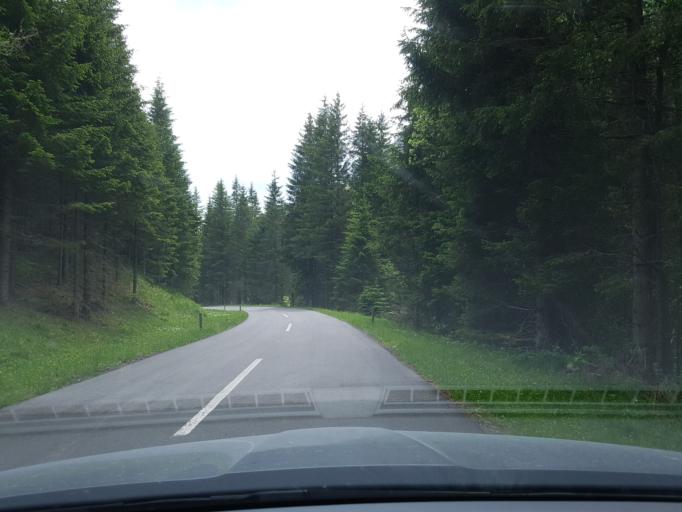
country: AT
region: Carinthia
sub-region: Politischer Bezirk Spittal an der Drau
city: Kleinkirchheim
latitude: 46.8885
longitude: 13.8423
